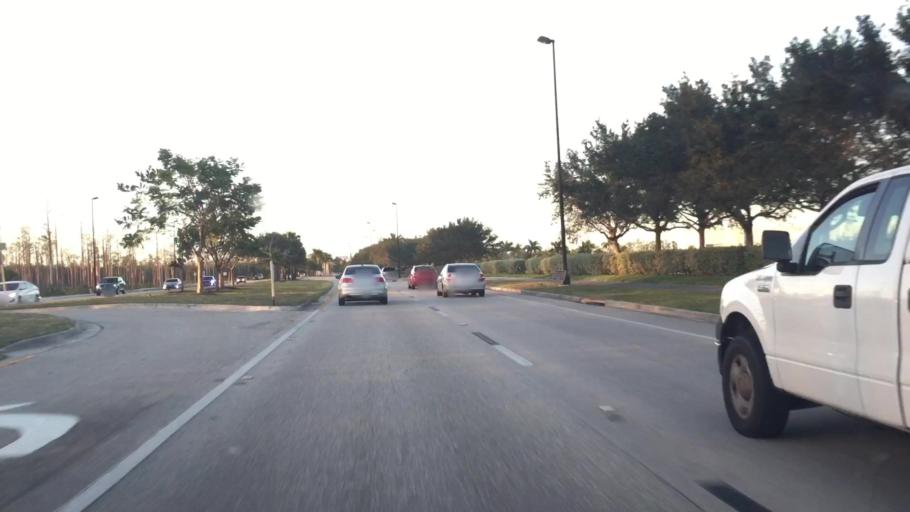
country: US
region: Florida
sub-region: Lee County
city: Three Oaks
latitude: 26.4992
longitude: -81.7840
